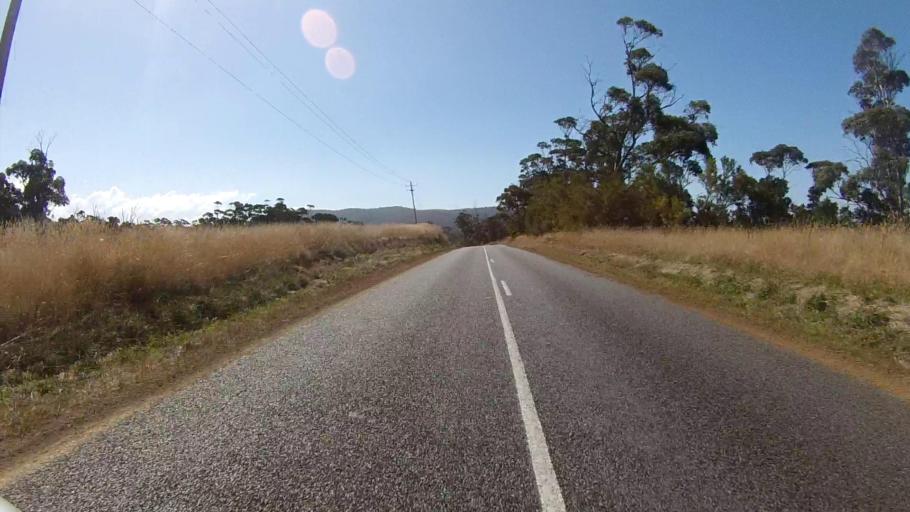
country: AU
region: Tasmania
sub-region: Sorell
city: Sorell
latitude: -42.2685
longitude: 148.0035
